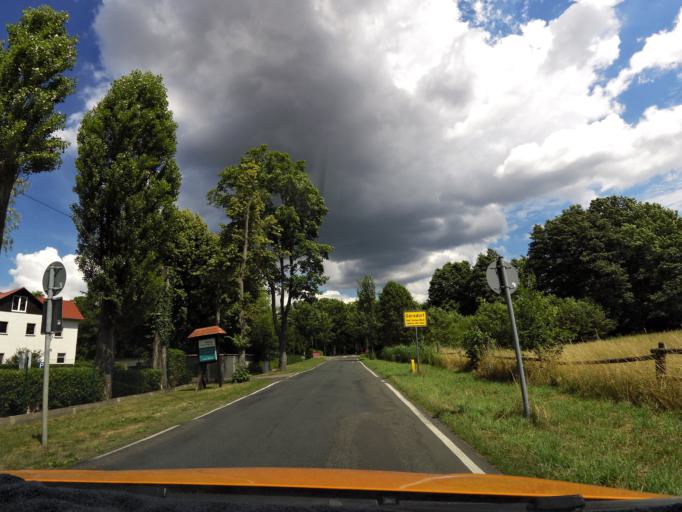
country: DE
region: Brandenburg
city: Munchehofe
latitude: 52.2440
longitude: 13.8321
